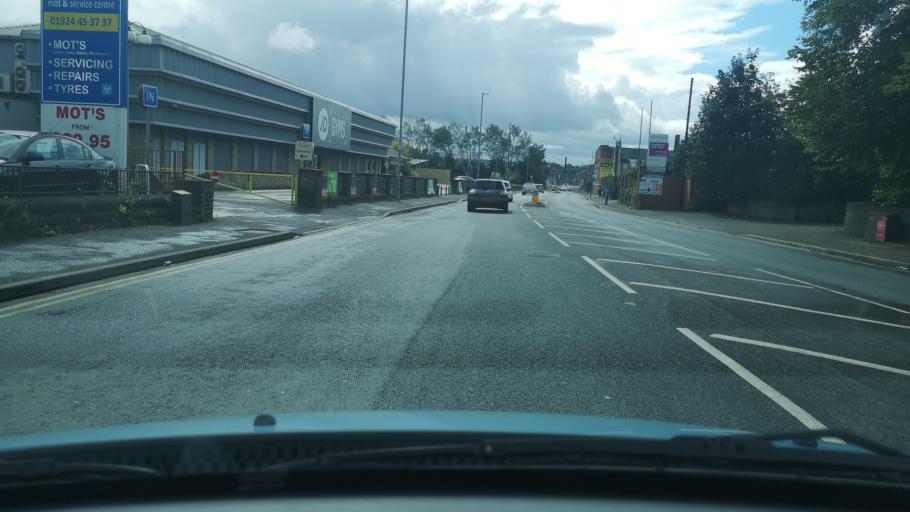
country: GB
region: England
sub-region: Kirklees
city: Batley
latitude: 53.7071
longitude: -1.6268
